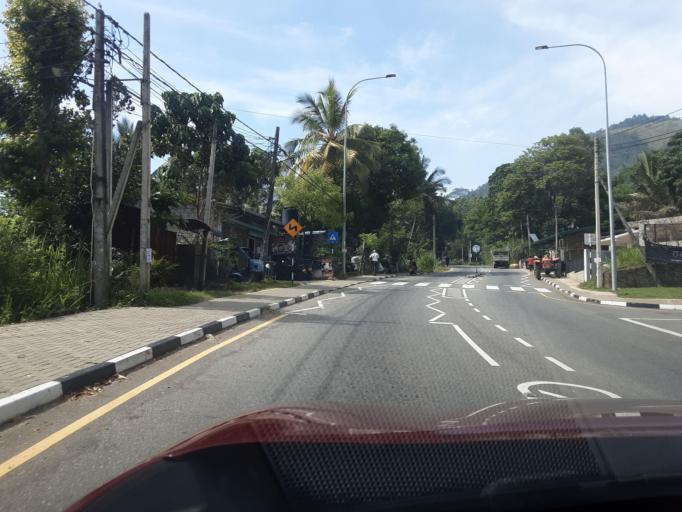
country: LK
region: Uva
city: Badulla
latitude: 6.9834
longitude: 81.0794
